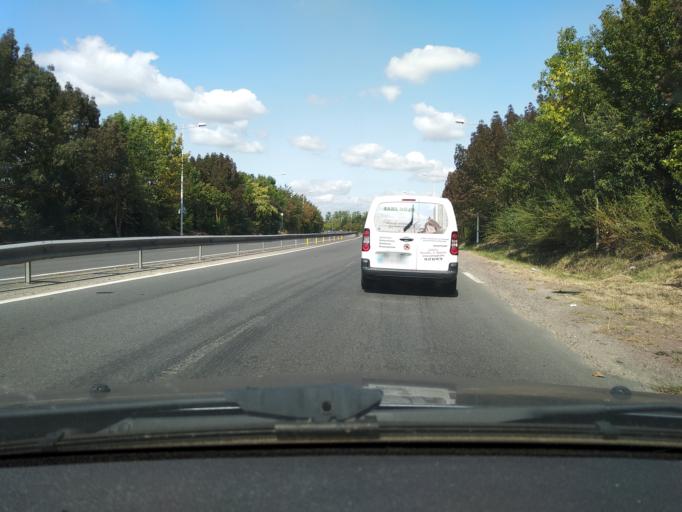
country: FR
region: Centre
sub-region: Departement d'Indre-et-Loire
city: Parcay-Meslay
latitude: 47.4203
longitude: 0.7168
